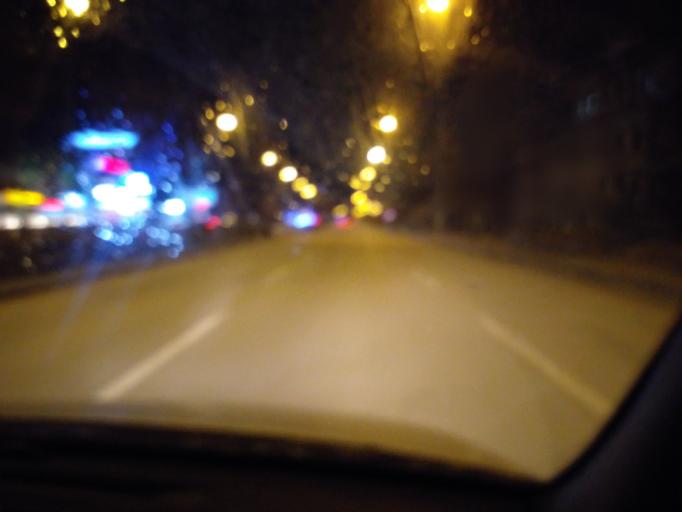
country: TR
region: Ankara
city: Batikent
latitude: 39.8834
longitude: 32.7137
